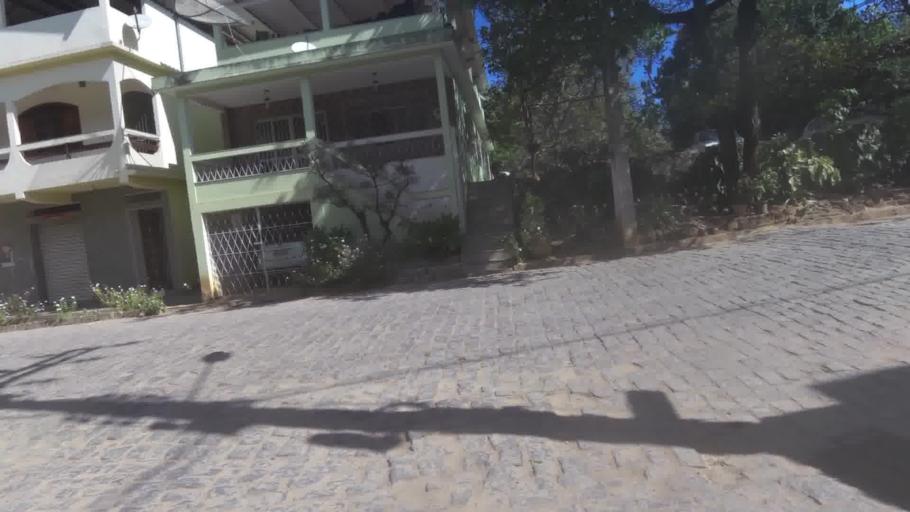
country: BR
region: Espirito Santo
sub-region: Vargem Alta
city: Vargem Alta
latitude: -20.6616
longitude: -41.0574
